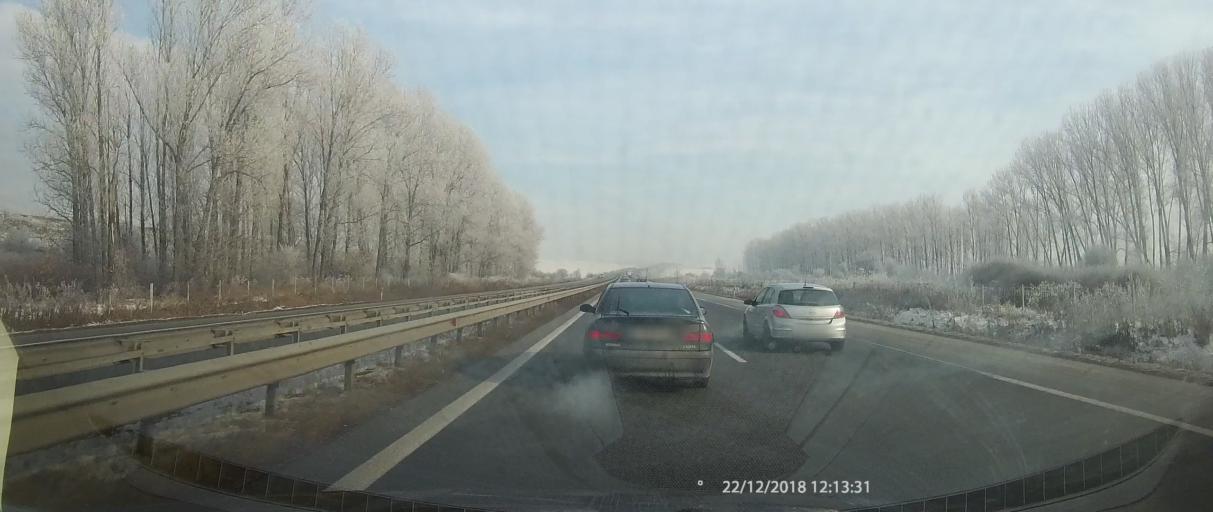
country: BG
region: Sofia-Capital
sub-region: Stolichna Obshtina
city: Bukhovo
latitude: 42.7195
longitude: 23.4962
